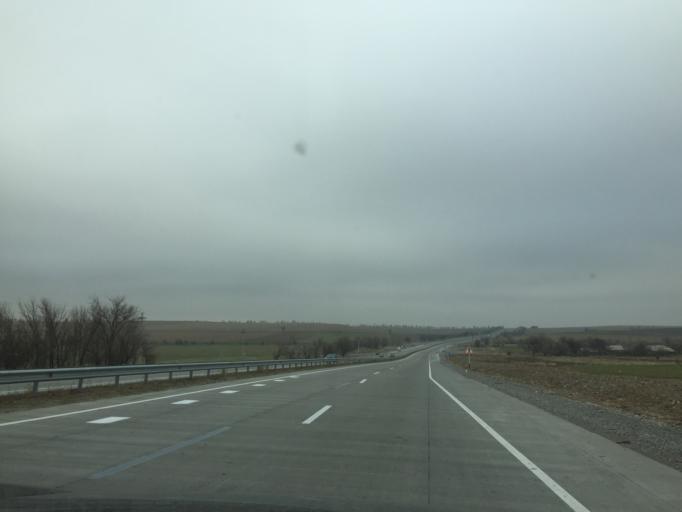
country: KZ
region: Ongtustik Qazaqstan
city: Aksu
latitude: 42.4793
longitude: 69.9135
